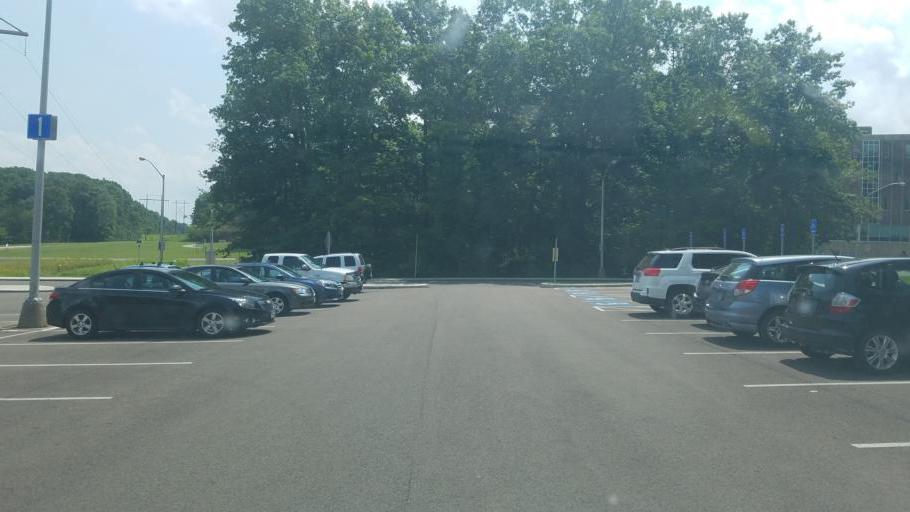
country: US
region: Ohio
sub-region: Richland County
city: Ontario
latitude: 40.7979
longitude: -82.5802
